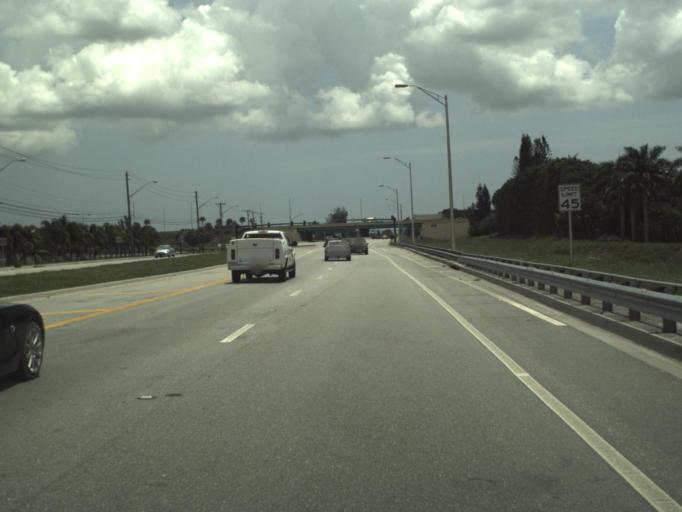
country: US
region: Florida
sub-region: Palm Beach County
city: Villages of Oriole
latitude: 26.4536
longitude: -80.1793
